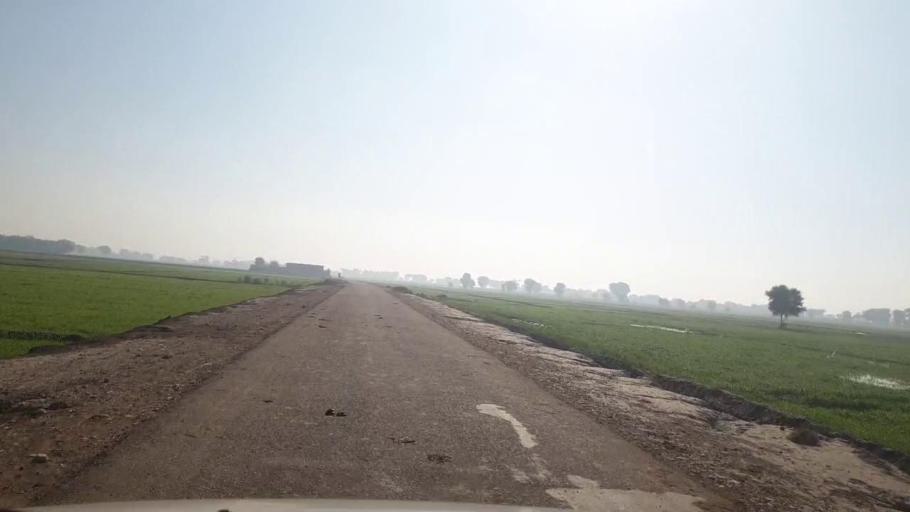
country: PK
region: Sindh
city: Dadu
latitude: 26.6409
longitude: 67.8276
